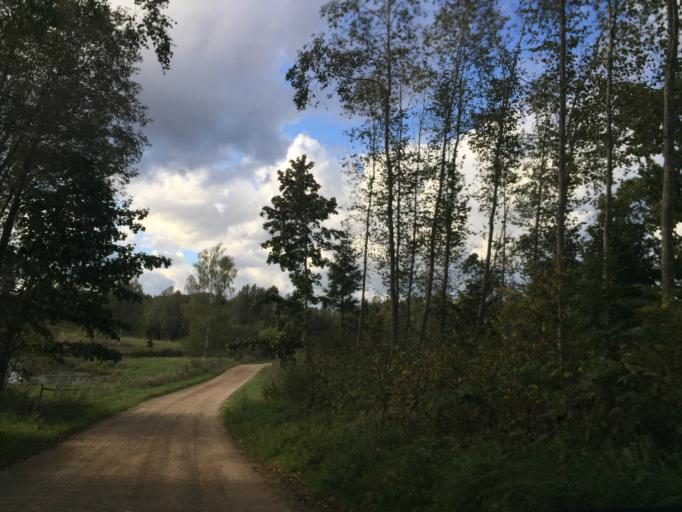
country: LV
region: Ligatne
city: Ligatne
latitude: 57.1335
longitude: 25.1001
